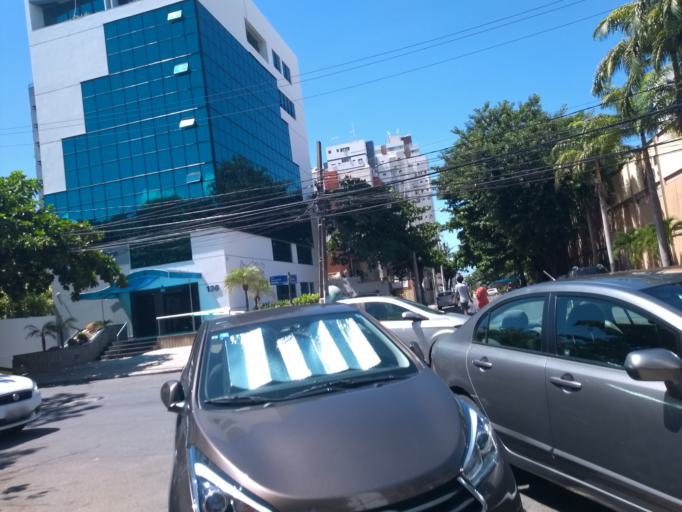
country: BR
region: Bahia
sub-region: Salvador
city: Salvador
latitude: -13.0012
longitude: -38.4574
